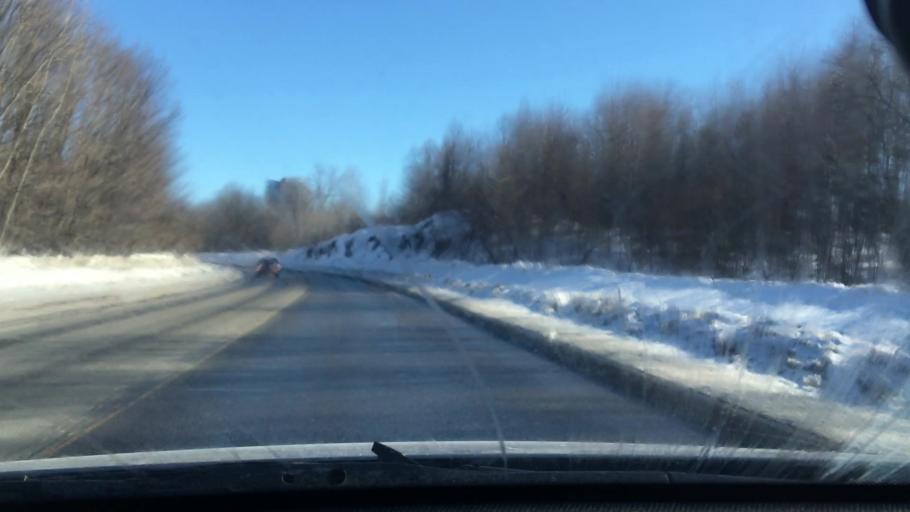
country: CA
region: Quebec
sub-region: Outaouais
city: Gatineau
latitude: 45.4486
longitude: -75.6457
